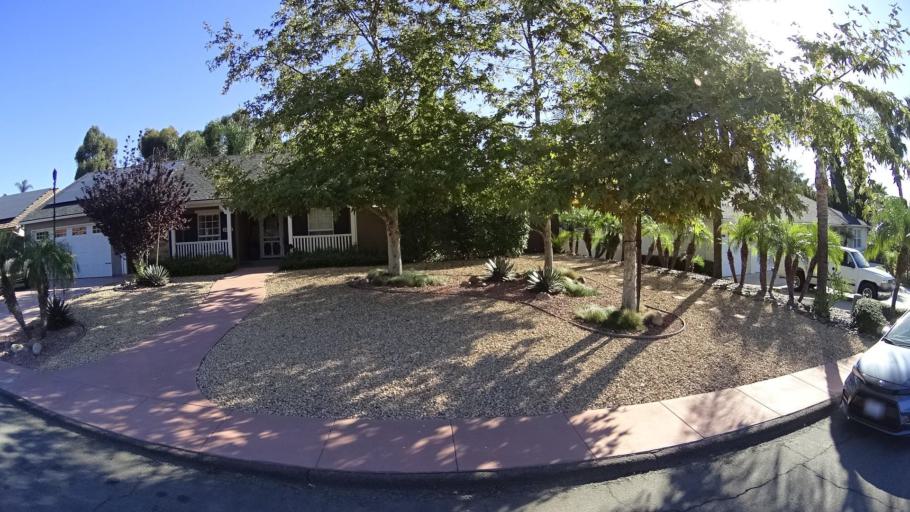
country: US
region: California
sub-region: San Diego County
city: Bonita
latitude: 32.6834
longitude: -117.0229
